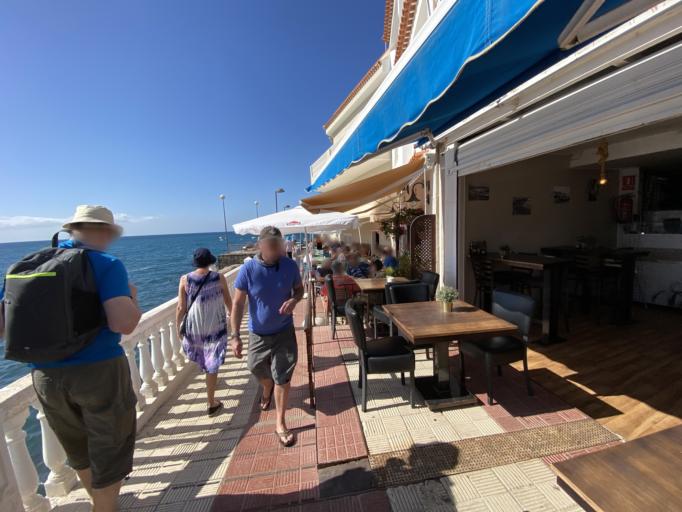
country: ES
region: Canary Islands
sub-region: Provincia de Santa Cruz de Tenerife
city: Adeje
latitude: 28.1008
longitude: -16.7560
